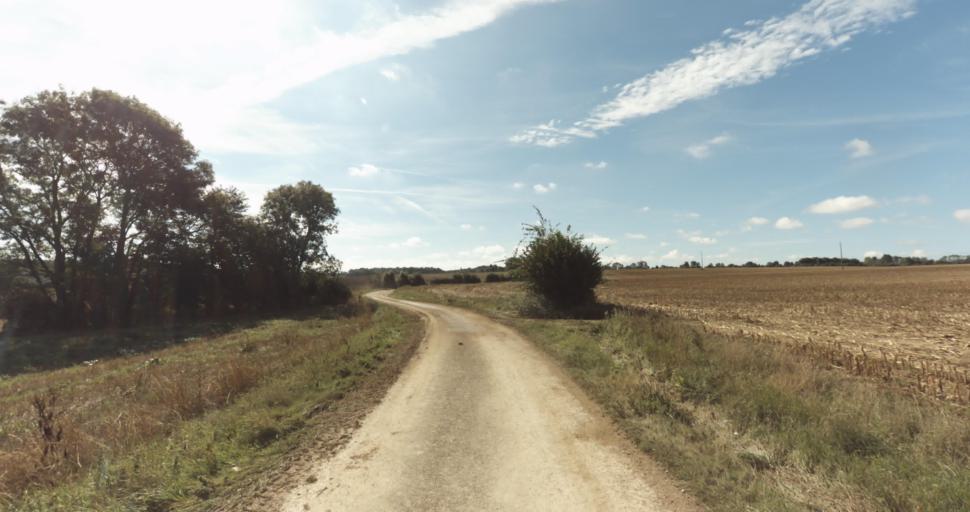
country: FR
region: Lower Normandy
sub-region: Departement du Calvados
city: Orbec
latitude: 48.9364
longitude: 0.3600
